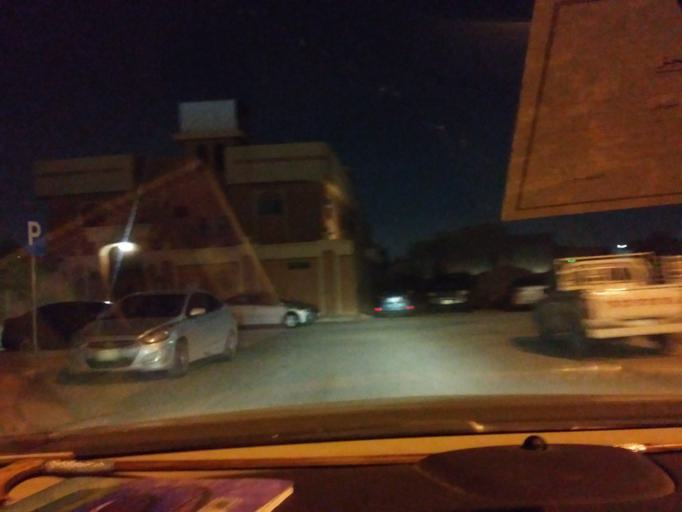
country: SA
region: Ar Riyad
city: Riyadh
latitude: 24.7438
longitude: 46.7570
